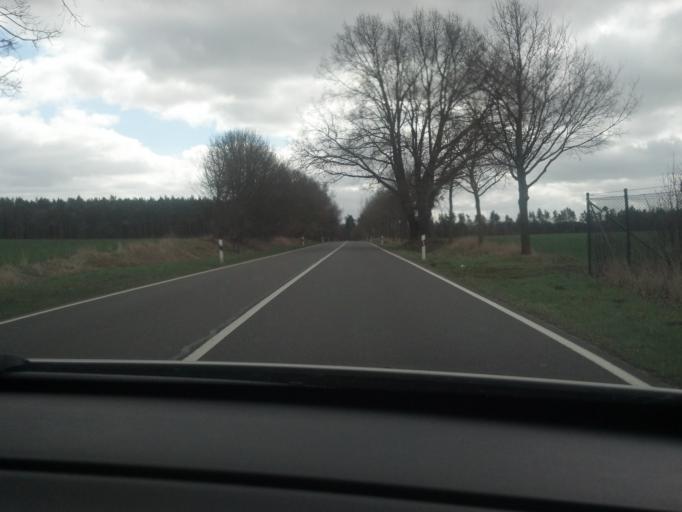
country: DE
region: Mecklenburg-Vorpommern
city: Rechlin
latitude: 53.3083
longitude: 12.7726
